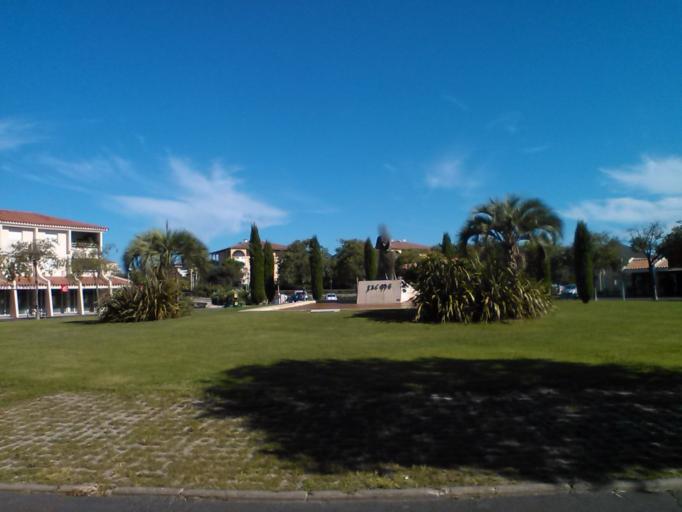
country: FR
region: Languedoc-Roussillon
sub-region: Departement de l'Herault
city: Lattes
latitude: 43.5697
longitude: 3.9042
